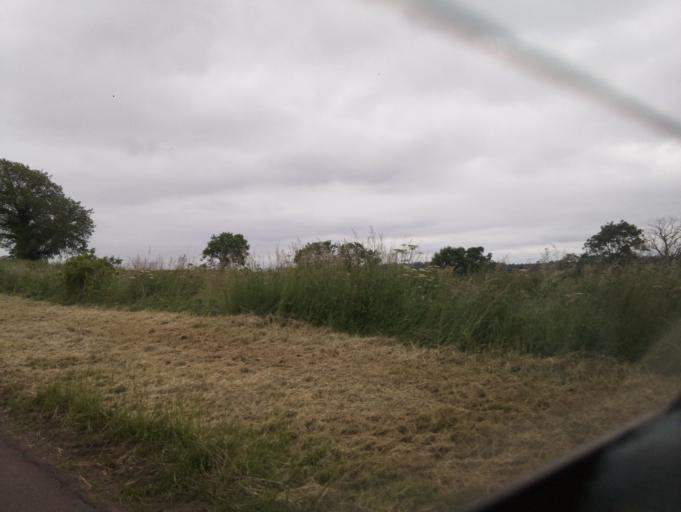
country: GB
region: England
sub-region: Leicestershire
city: Melton Mowbray
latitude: 52.7008
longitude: -0.8389
